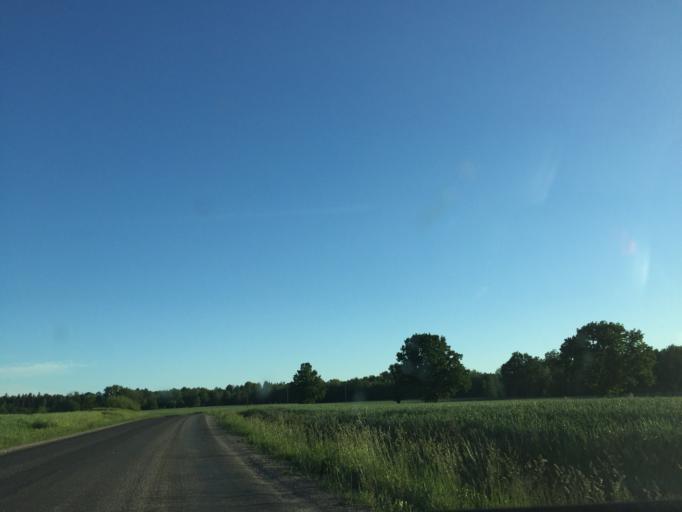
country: LV
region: Broceni
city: Broceni
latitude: 56.7401
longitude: 22.5107
